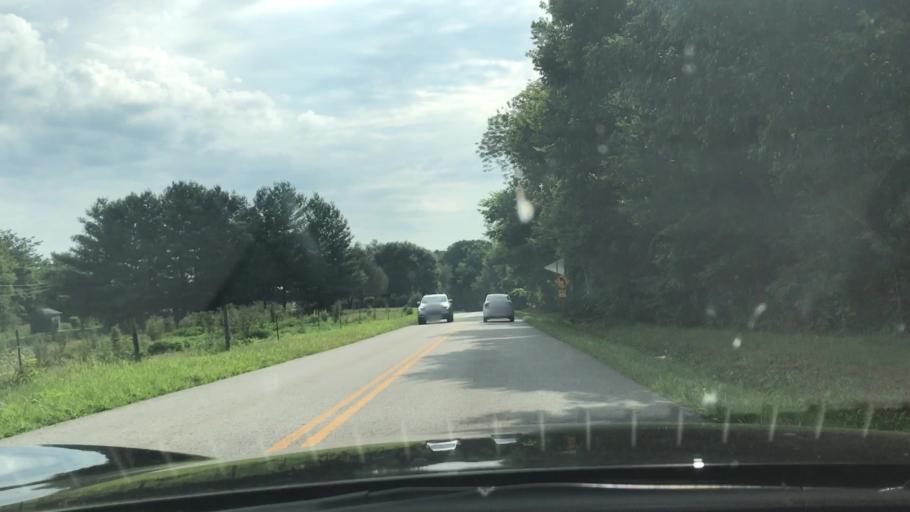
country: US
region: Kentucky
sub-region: Green County
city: Greensburg
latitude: 37.2630
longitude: -85.5498
